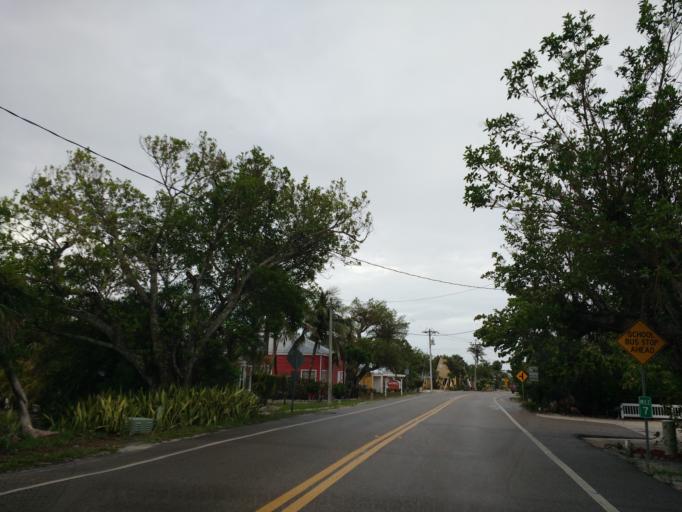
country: US
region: Florida
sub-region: Lee County
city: Saint James City
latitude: 26.4820
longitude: -82.1810
